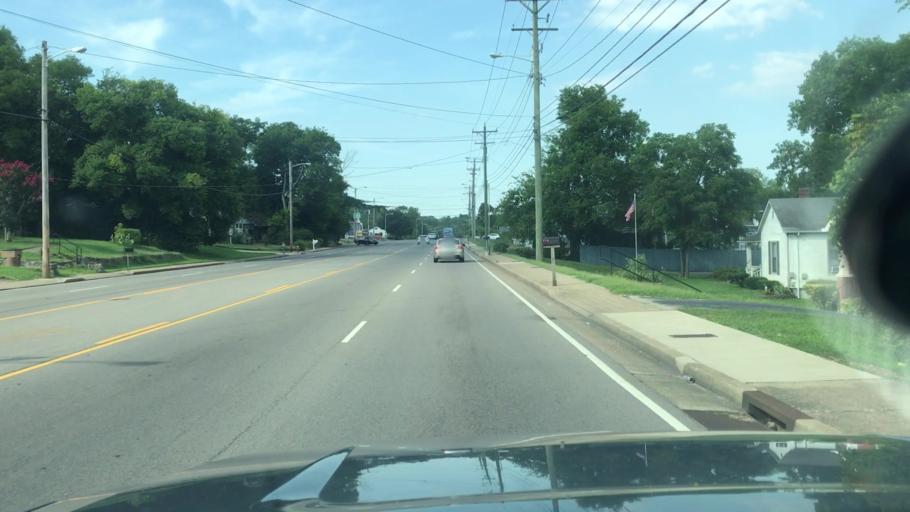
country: US
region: Tennessee
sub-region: Davidson County
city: Nashville
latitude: 36.1957
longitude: -86.8293
